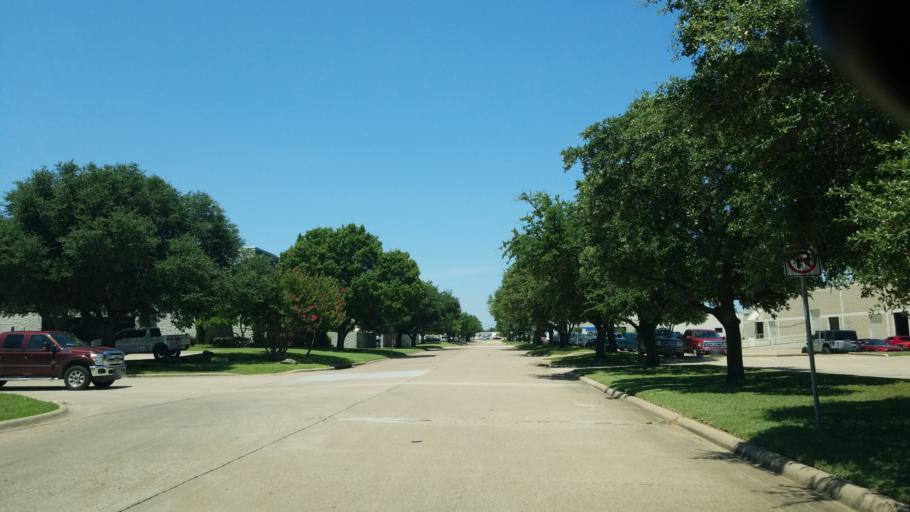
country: US
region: Texas
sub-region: Dallas County
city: Farmers Branch
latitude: 32.9225
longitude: -96.9269
